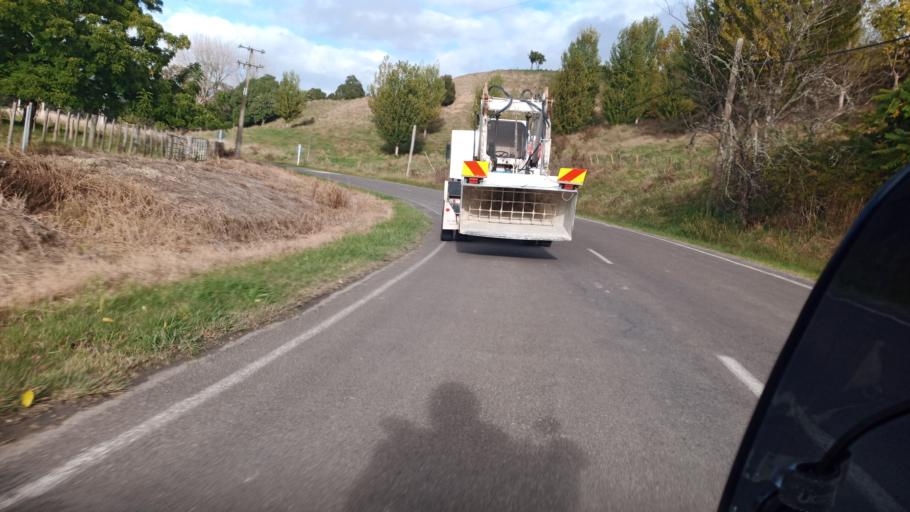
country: NZ
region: Gisborne
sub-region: Gisborne District
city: Gisborne
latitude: -38.5854
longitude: 177.7866
